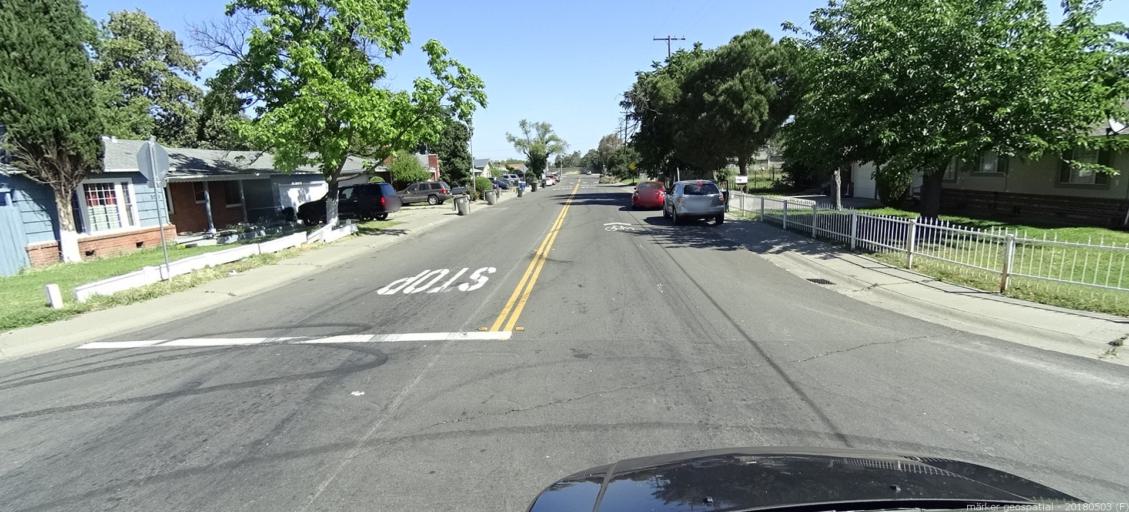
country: US
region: California
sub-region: Sacramento County
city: Arden-Arcade
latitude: 38.6347
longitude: -121.4161
